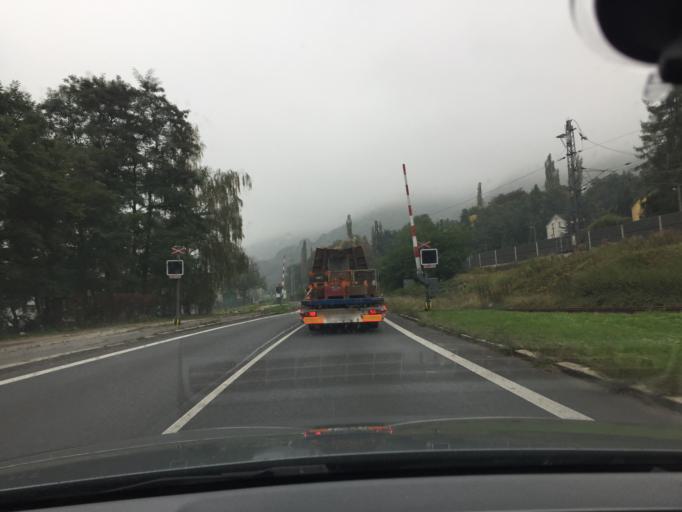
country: CZ
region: Ustecky
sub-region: Okres Usti nad Labem
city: Usti nad Labem
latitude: 50.6403
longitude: 14.0458
